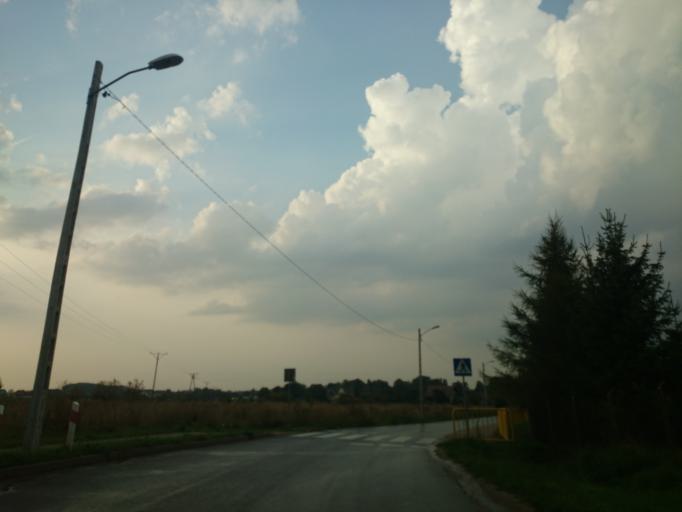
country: PL
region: West Pomeranian Voivodeship
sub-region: Powiat policki
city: Przeclaw
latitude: 53.3805
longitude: 14.4681
